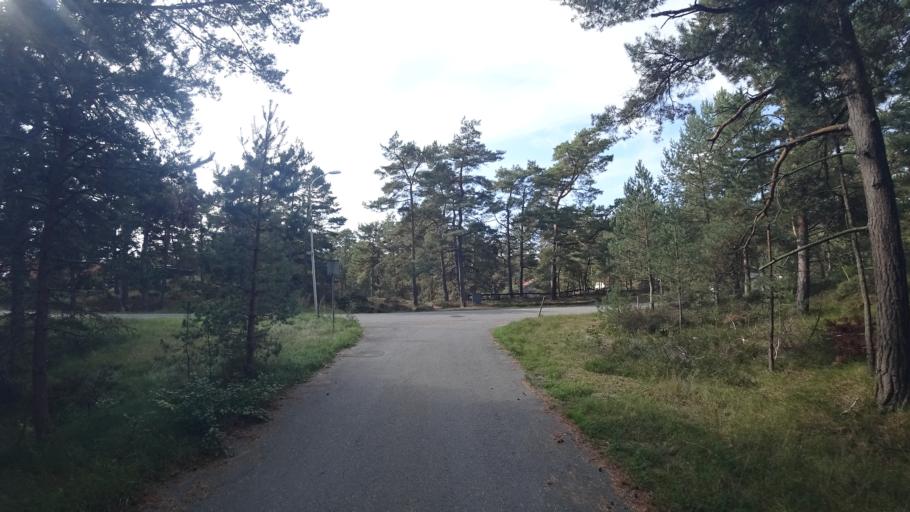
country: SE
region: Skane
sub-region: Kristianstads Kommun
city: Ahus
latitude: 55.9110
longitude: 14.2909
